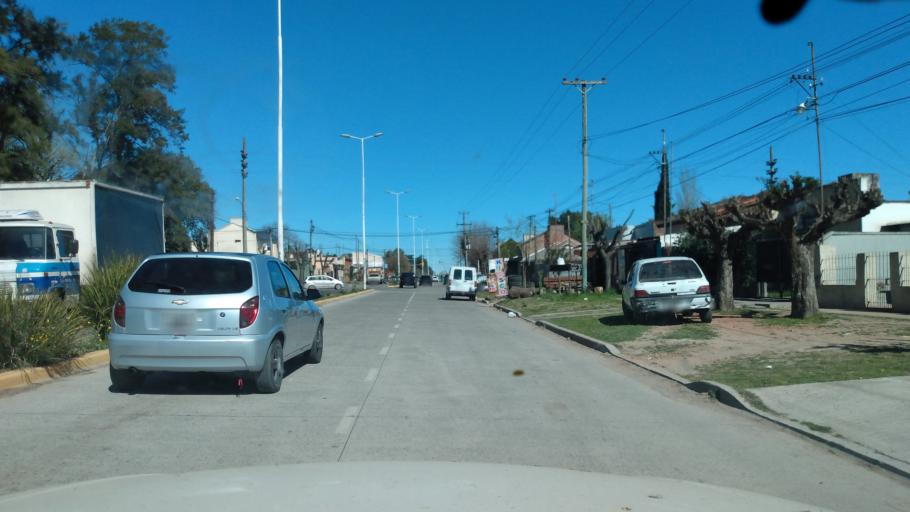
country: AR
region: Buenos Aires
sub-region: Partido de Lujan
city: Lujan
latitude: -34.5573
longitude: -59.1021
